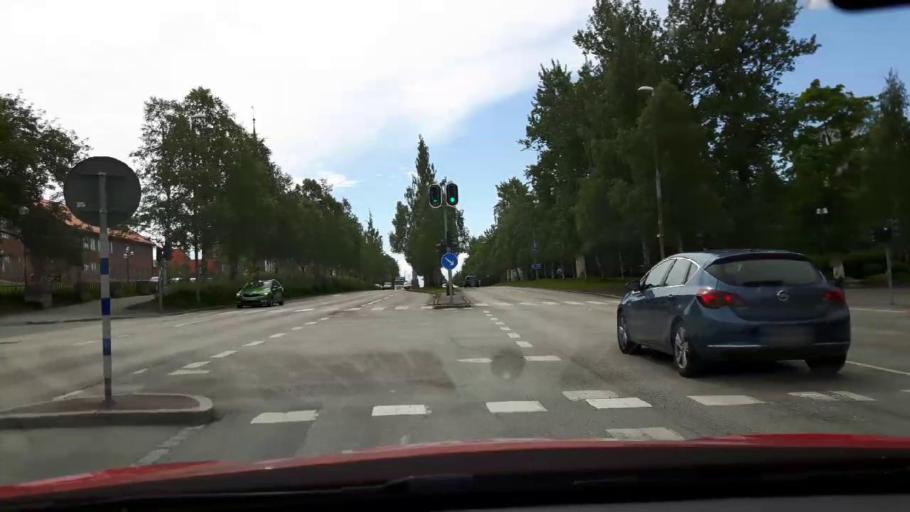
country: SE
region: Jaemtland
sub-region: OEstersunds Kommun
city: Ostersund
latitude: 63.1361
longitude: 14.4610
